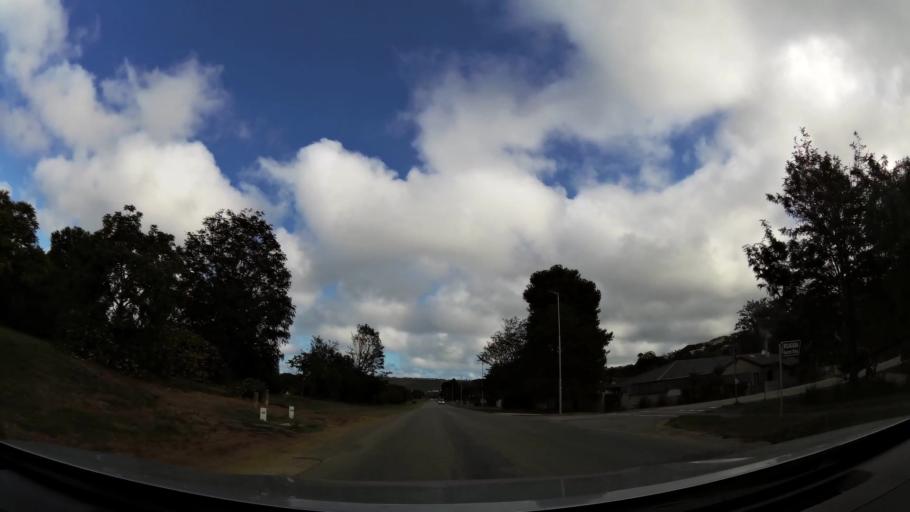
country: ZA
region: Western Cape
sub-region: Eden District Municipality
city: Plettenberg Bay
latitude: -34.0707
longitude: 23.3685
